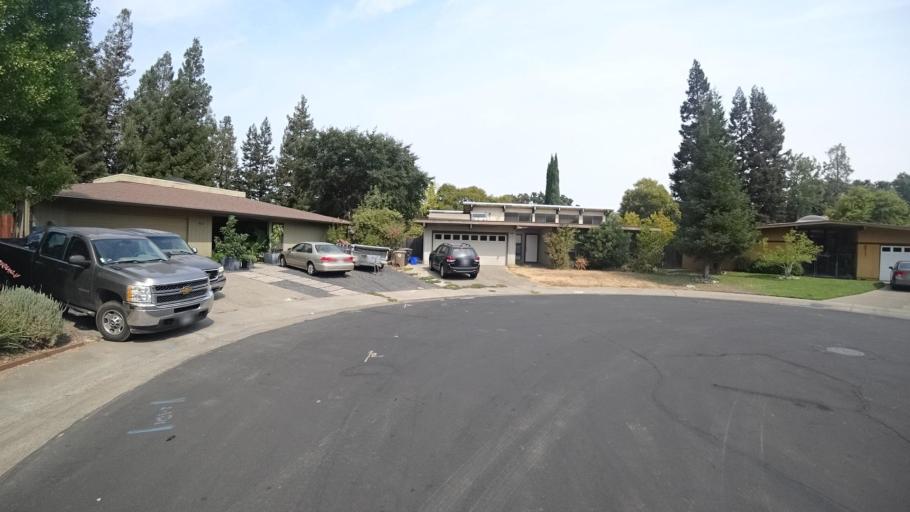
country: US
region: California
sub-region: Sacramento County
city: Elk Grove
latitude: 38.4150
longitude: -121.3751
